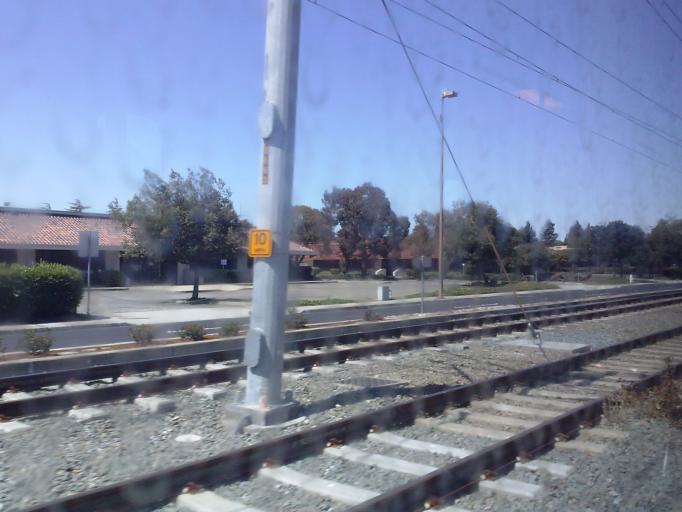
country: US
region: California
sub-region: Santa Clara County
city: Santa Clara
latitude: 37.4034
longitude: -121.9817
